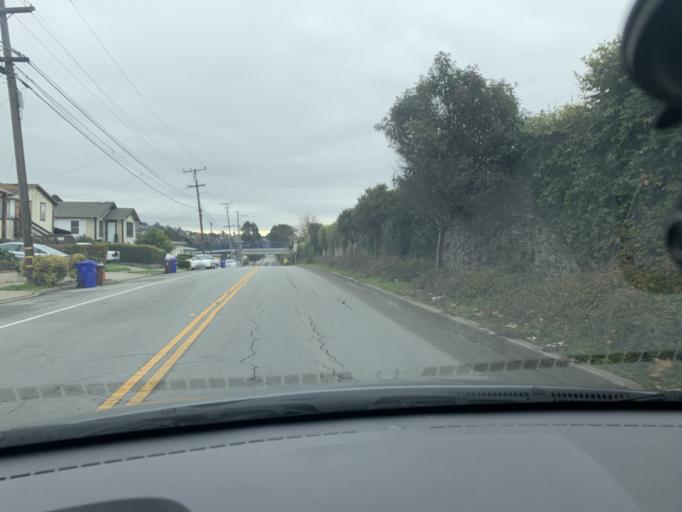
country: US
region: California
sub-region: Contra Costa County
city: Rollingwood
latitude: 37.9549
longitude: -122.3287
